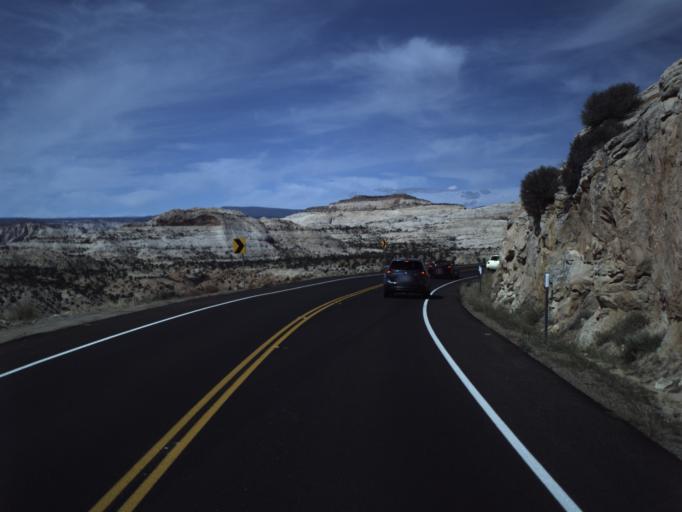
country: US
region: Utah
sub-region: Wayne County
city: Loa
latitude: 37.8125
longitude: -111.4077
